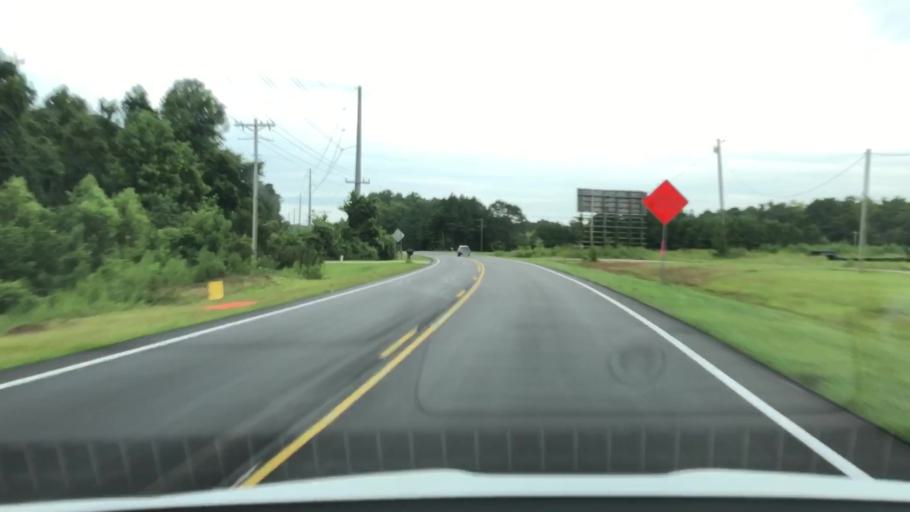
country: US
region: North Carolina
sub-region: Onslow County
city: Swansboro
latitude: 34.8012
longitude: -77.1318
